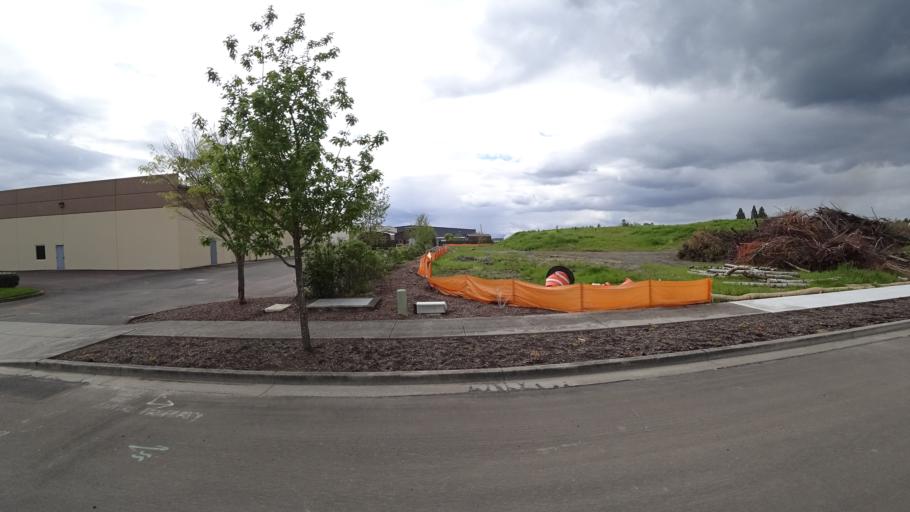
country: US
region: Oregon
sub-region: Washington County
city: Hillsboro
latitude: 45.5484
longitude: -122.9457
